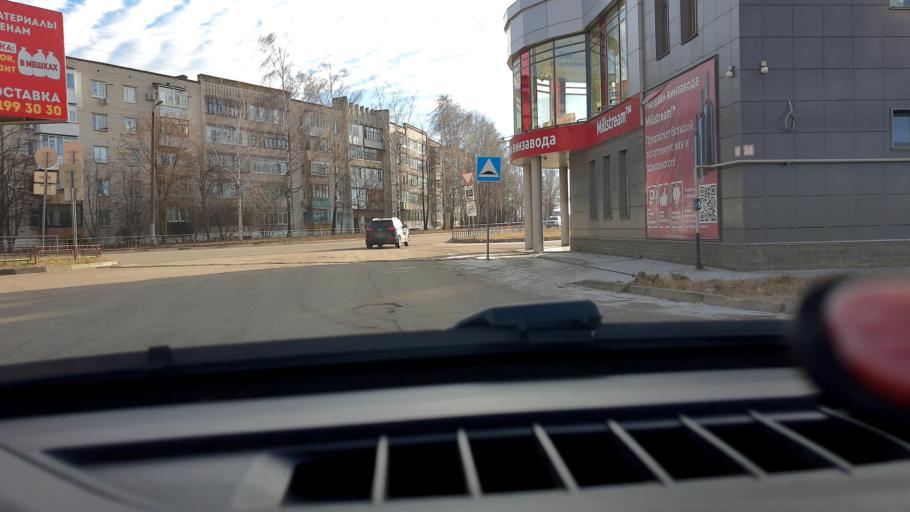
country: RU
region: Nizjnij Novgorod
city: Kstovo
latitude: 56.1457
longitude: 44.1784
